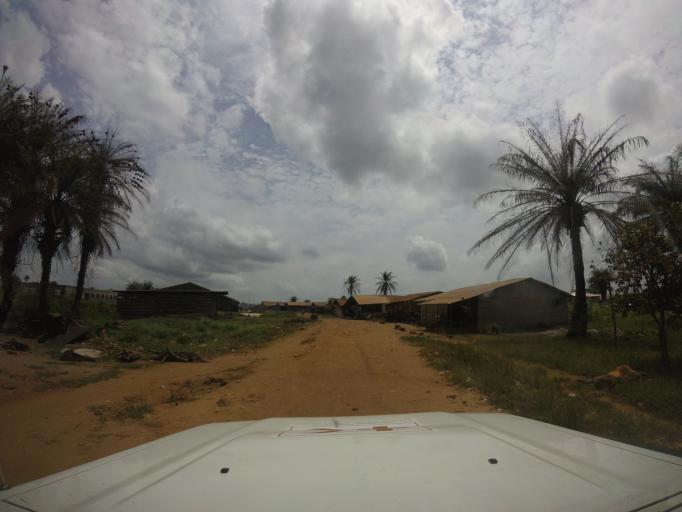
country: LR
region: Grand Cape Mount
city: Robertsport
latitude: 6.7563
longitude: -11.3555
